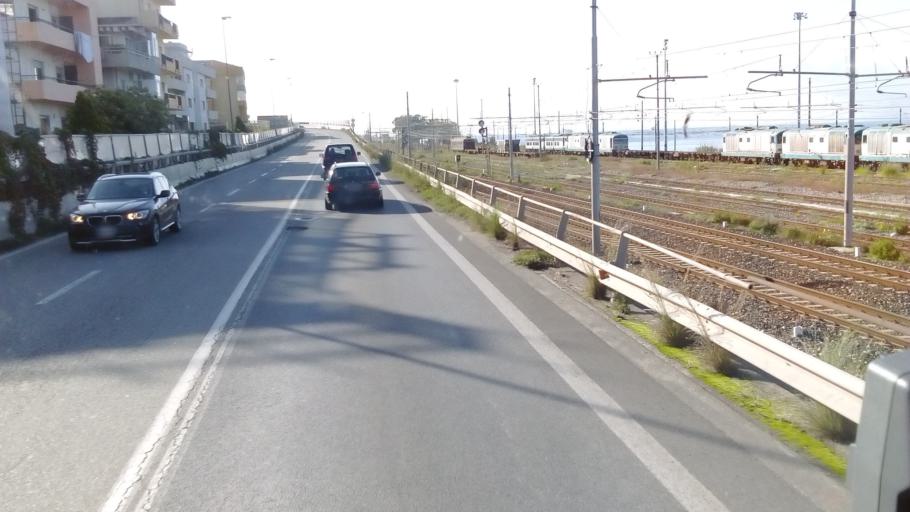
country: IT
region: Calabria
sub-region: Provincia di Reggio Calabria
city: Campo Calabro
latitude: 38.2093
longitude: 15.6355
